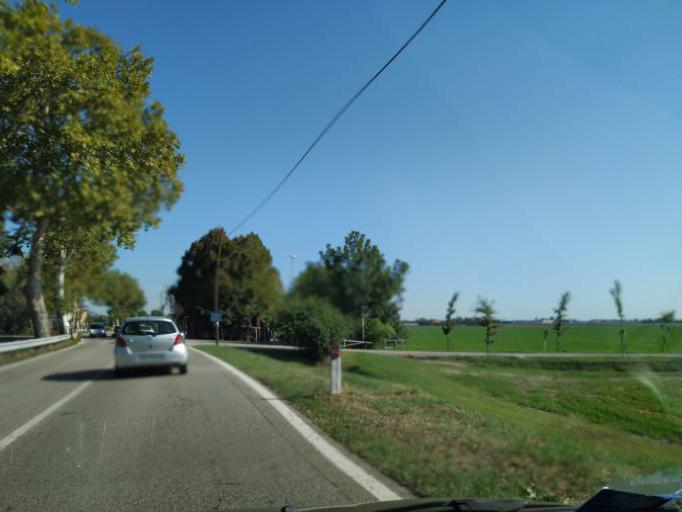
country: IT
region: Emilia-Romagna
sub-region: Provincia di Bologna
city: Decima
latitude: 44.6864
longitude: 11.2193
